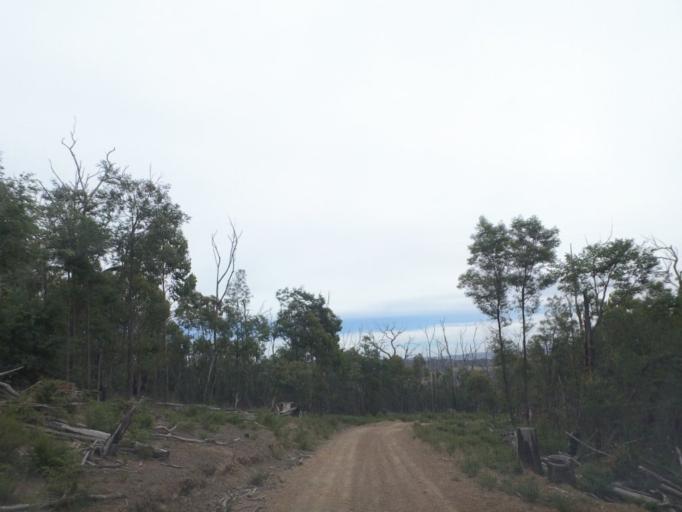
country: AU
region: Victoria
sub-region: Murrindindi
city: Alexandra
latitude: -37.3784
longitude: 145.5629
